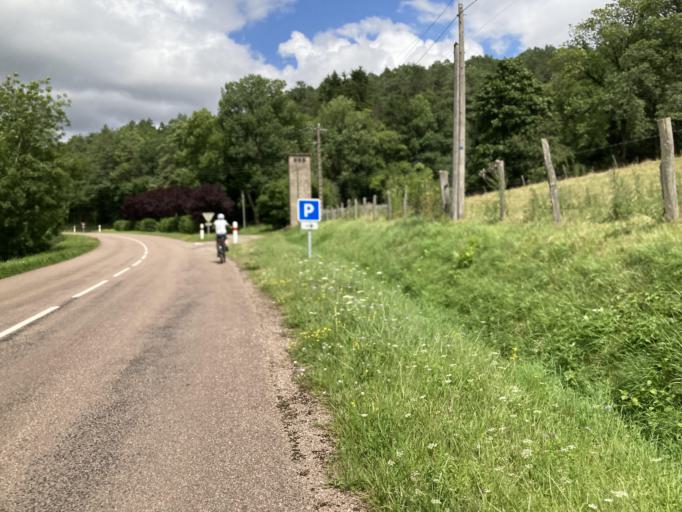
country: FR
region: Bourgogne
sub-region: Departement de la Cote-d'Or
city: Montbard
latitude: 47.6333
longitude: 4.3738
